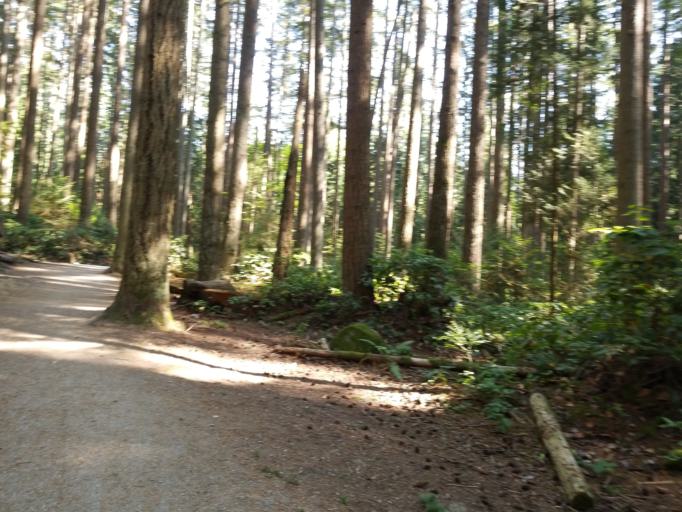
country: CA
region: British Columbia
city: West End
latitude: 49.2515
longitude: -123.2164
